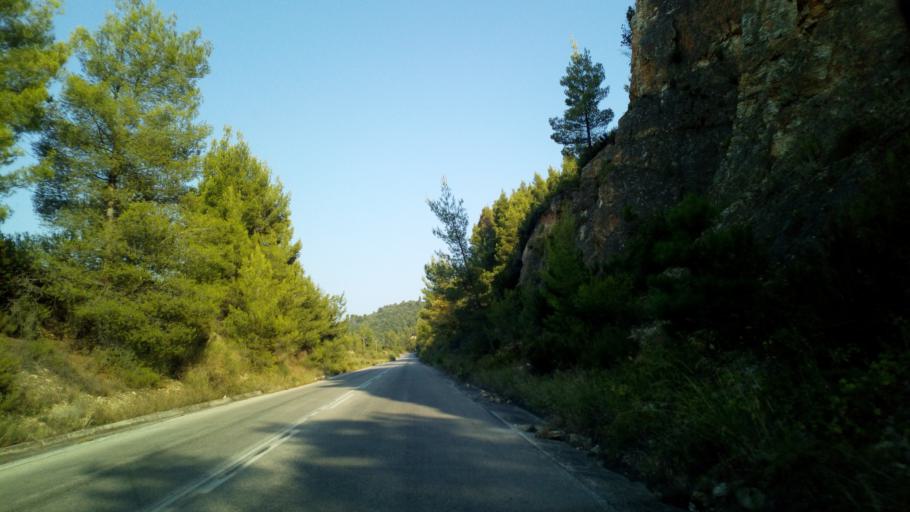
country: GR
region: Central Macedonia
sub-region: Nomos Chalkidikis
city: Neos Marmaras
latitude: 40.1634
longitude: 23.8666
